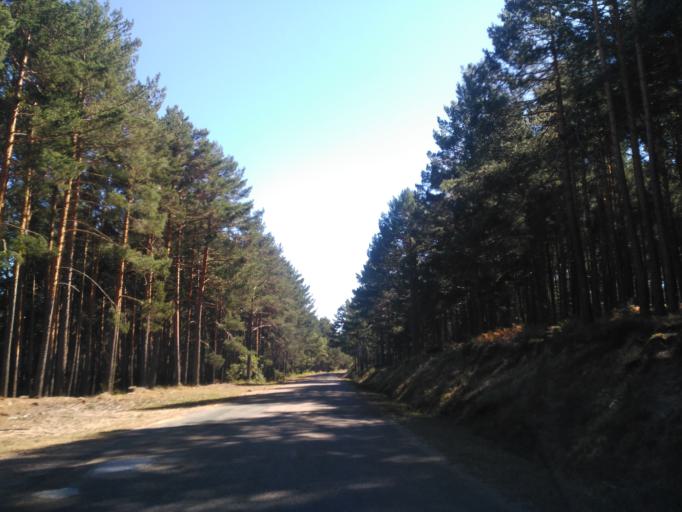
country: ES
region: Castille and Leon
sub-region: Provincia de Soria
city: Vinuesa
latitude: 41.9675
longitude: -2.7910
